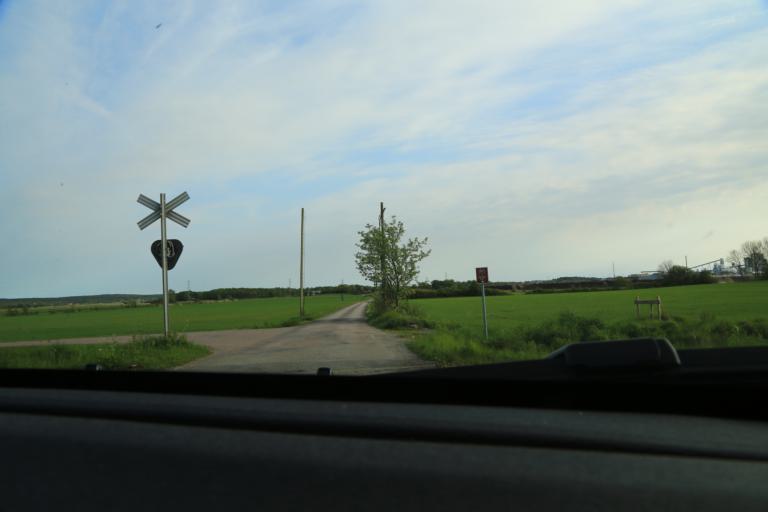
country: SE
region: Halland
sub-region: Kungsbacka Kommun
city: Frillesas
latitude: 57.2396
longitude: 12.1908
